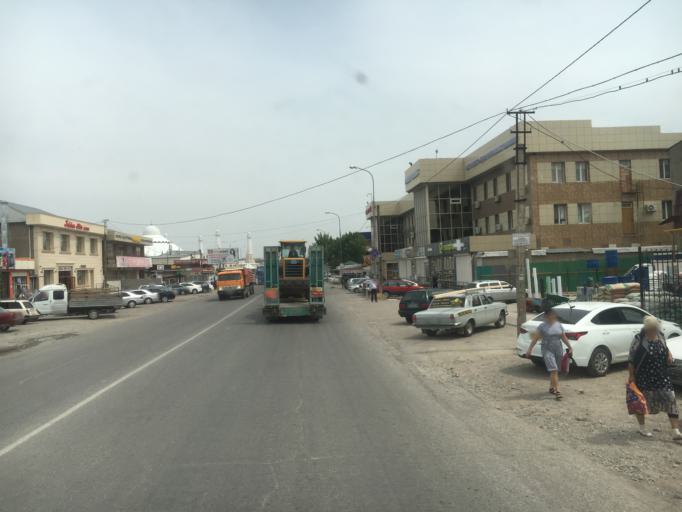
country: KZ
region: Ongtustik Qazaqstan
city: Shymkent
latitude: 42.3478
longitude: 69.5276
